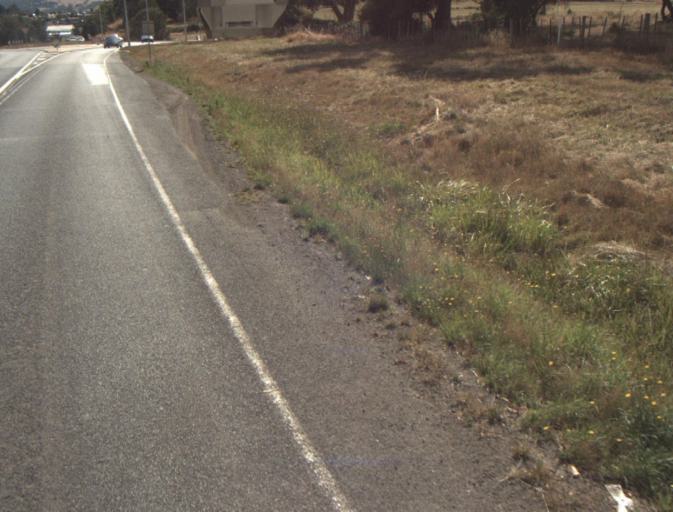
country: AU
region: Tasmania
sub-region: Launceston
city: Summerhill
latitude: -41.4819
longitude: 147.1553
